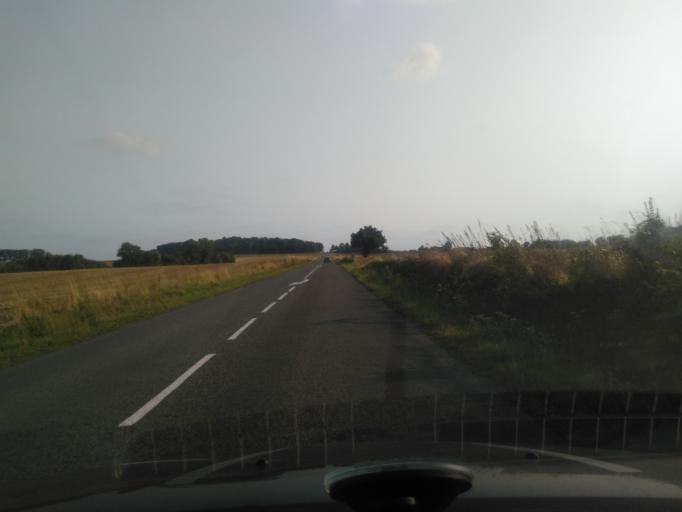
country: FR
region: Picardie
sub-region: Departement de l'Aisne
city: Bruyeres-et-Montberault
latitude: 49.5084
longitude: 3.6741
